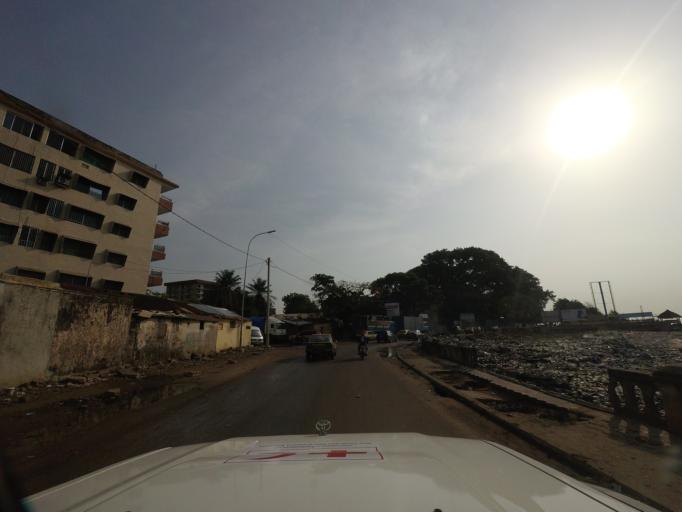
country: GN
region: Conakry
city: Camayenne
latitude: 9.5173
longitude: -13.6955
